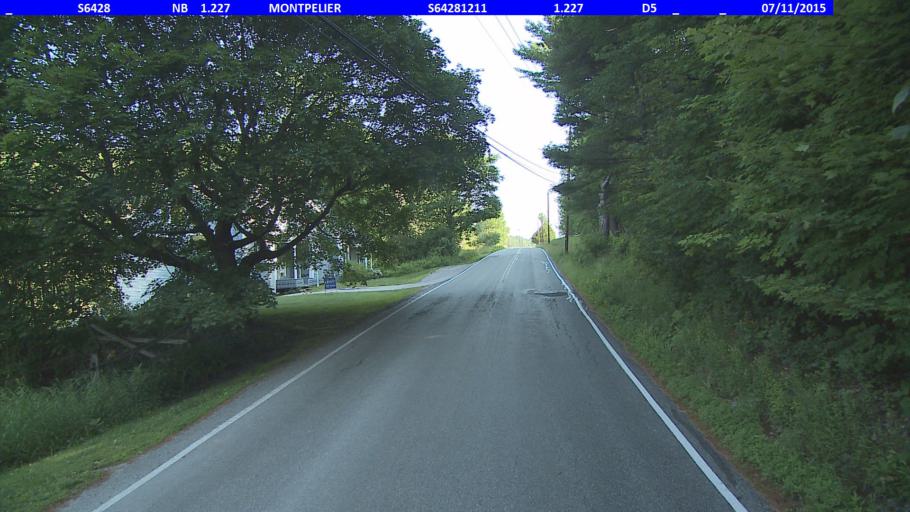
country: US
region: Vermont
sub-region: Washington County
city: Montpelier
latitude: 44.2789
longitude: -72.5934
